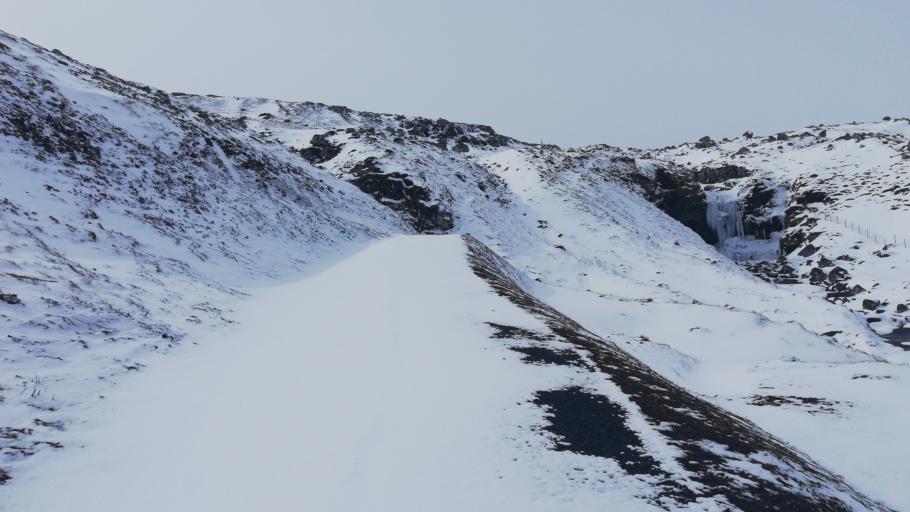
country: FO
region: Streymoy
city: Hoyvik
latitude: 62.0315
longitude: -6.8099
